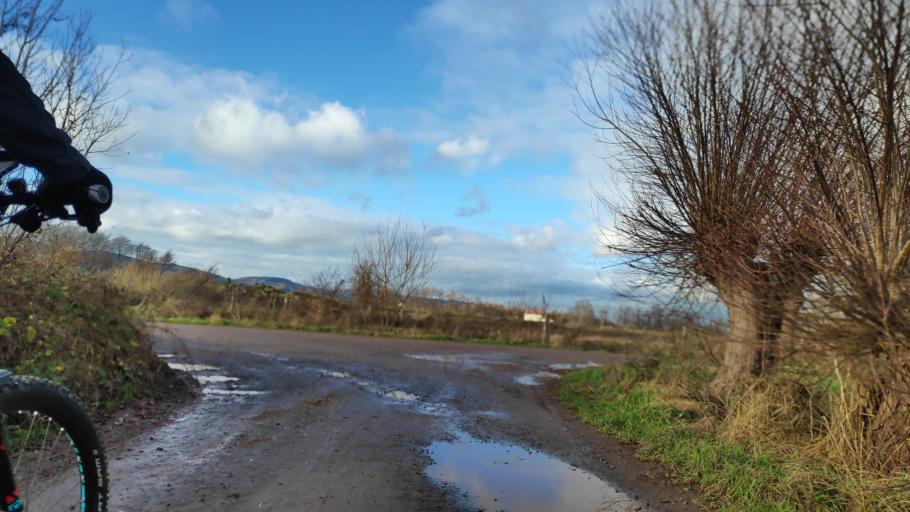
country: DE
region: North Rhine-Westphalia
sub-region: Regierungsbezirk Detmold
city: Minden
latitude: 52.2766
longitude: 8.8528
